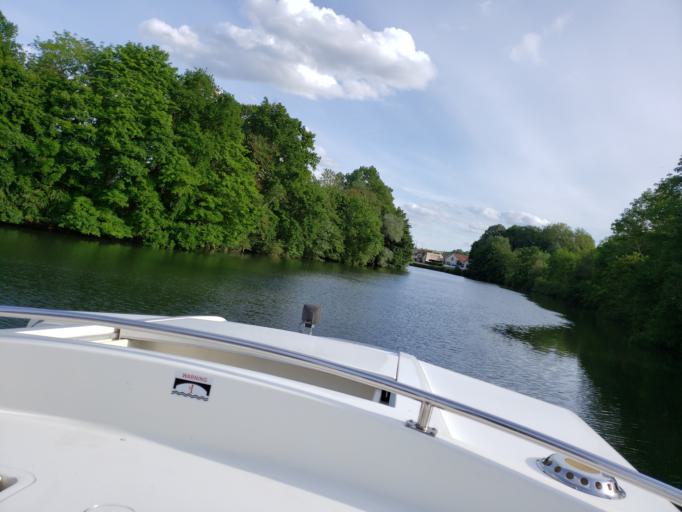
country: FR
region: Bourgogne
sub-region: Departement de l'Yonne
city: Cheny
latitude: 47.9313
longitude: 3.5162
